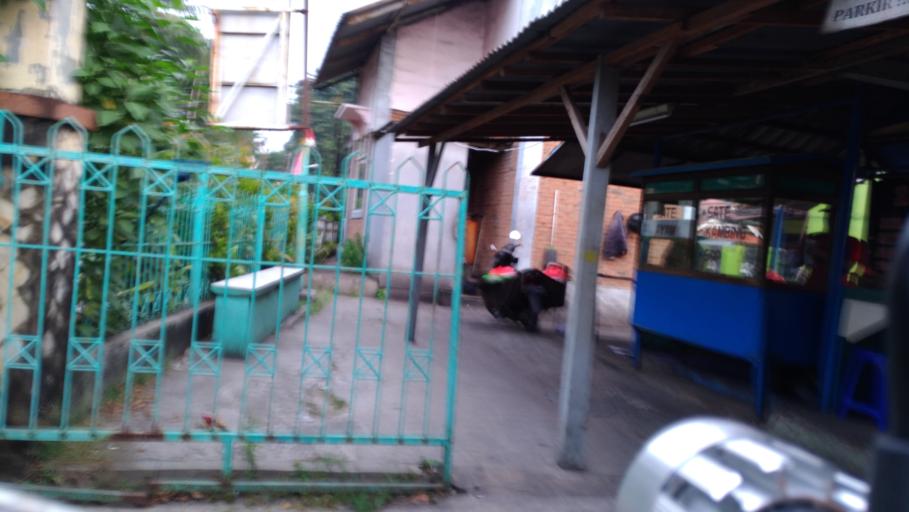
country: ID
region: West Java
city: Depok
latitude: -6.3648
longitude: 106.8657
